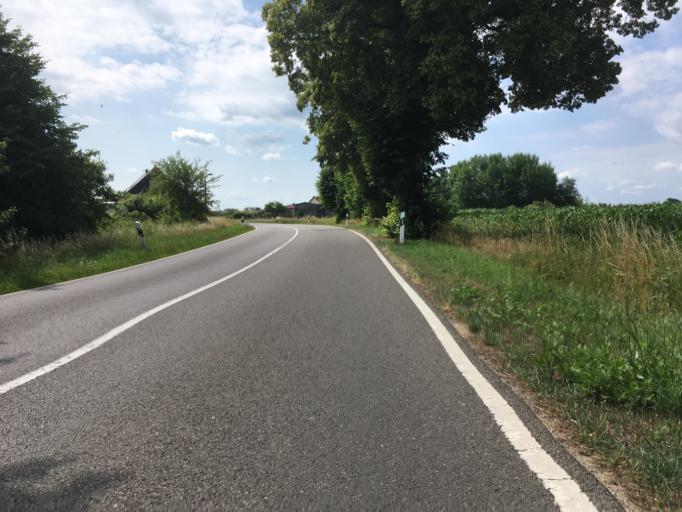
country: DE
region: Brandenburg
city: Friedrichswalde
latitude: 53.0356
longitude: 13.7114
